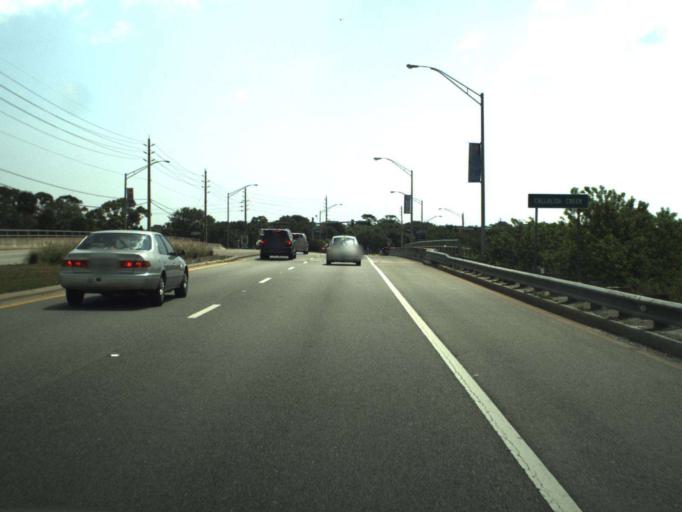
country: US
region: Florida
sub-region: Volusia County
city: New Smyrna Beach
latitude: 29.0286
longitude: -80.9049
